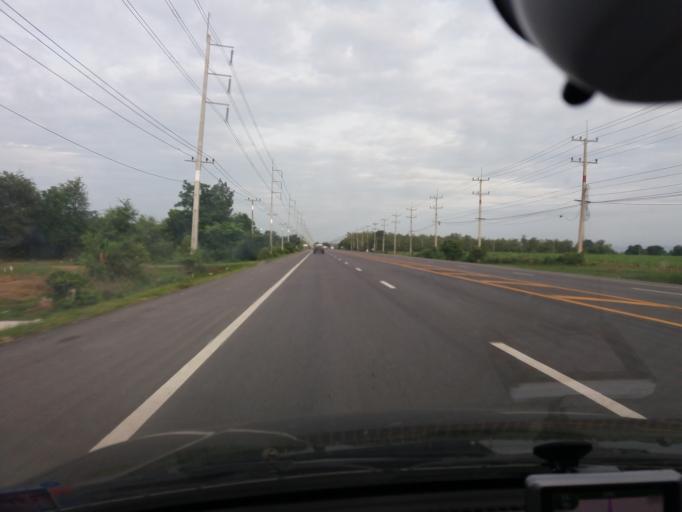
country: TH
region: Suphan Buri
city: U Thong
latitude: 14.3364
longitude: 99.8145
